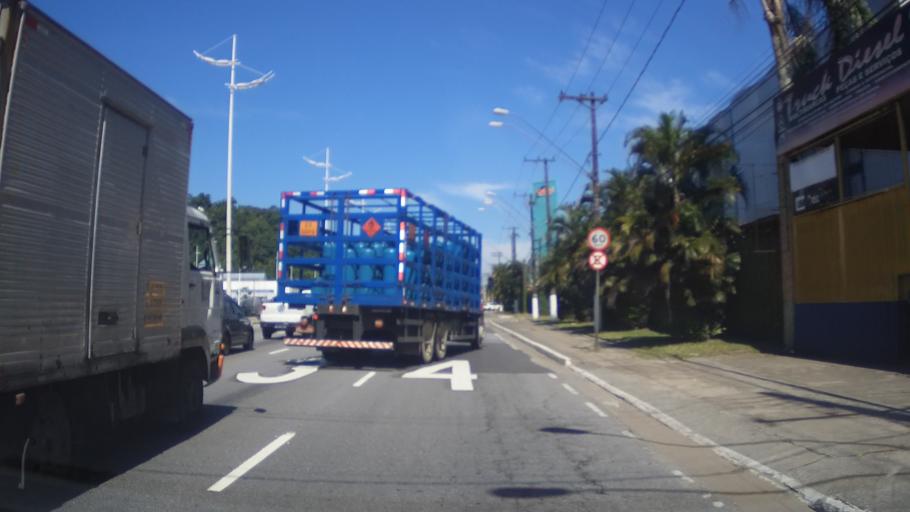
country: BR
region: Sao Paulo
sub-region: Praia Grande
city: Praia Grande
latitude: -23.9939
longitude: -46.4062
